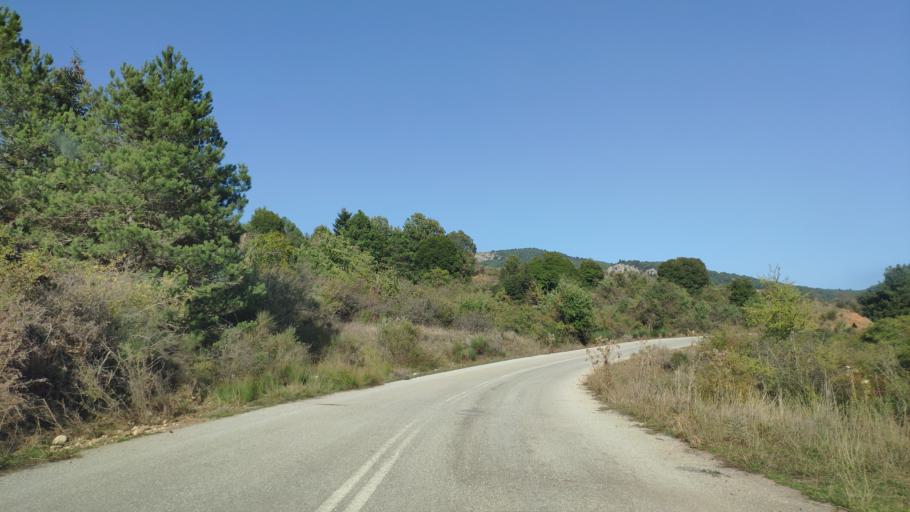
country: GR
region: West Greece
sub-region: Nomos Achaias
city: Aiyira
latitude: 38.0059
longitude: 22.3973
